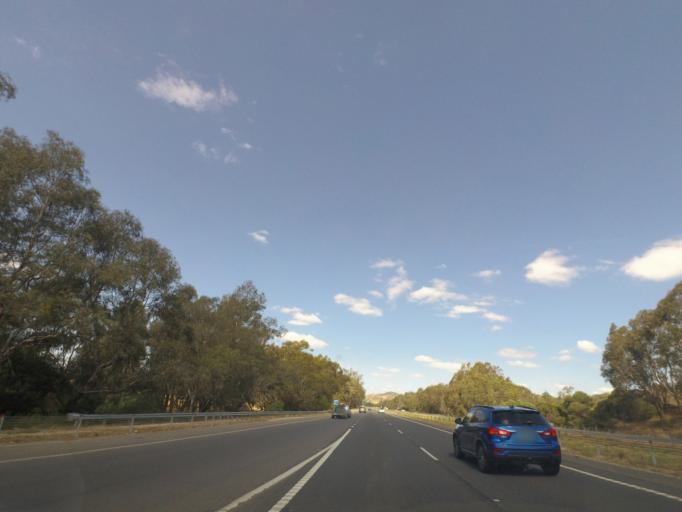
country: AU
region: Victoria
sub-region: Wodonga
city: Wodonga
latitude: -36.1078
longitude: 146.8739
